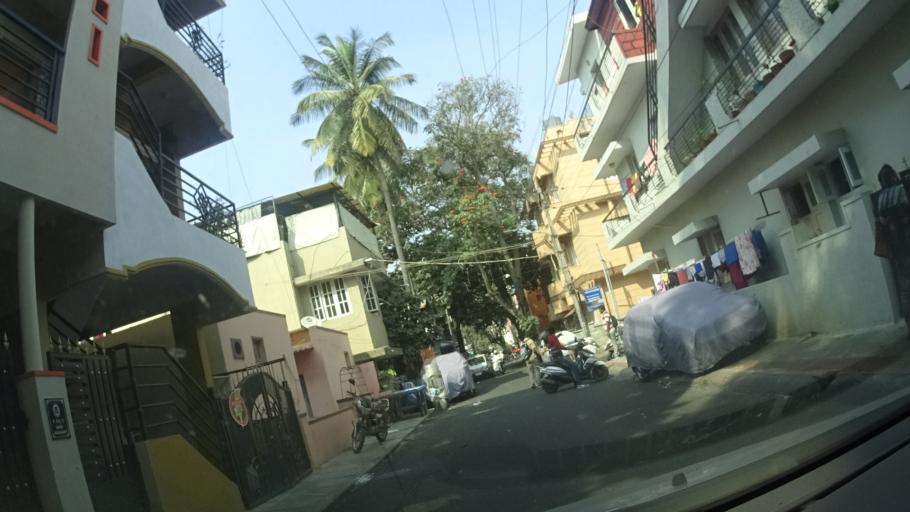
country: IN
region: Karnataka
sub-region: Bangalore Urban
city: Bangalore
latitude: 12.9428
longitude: 77.5597
